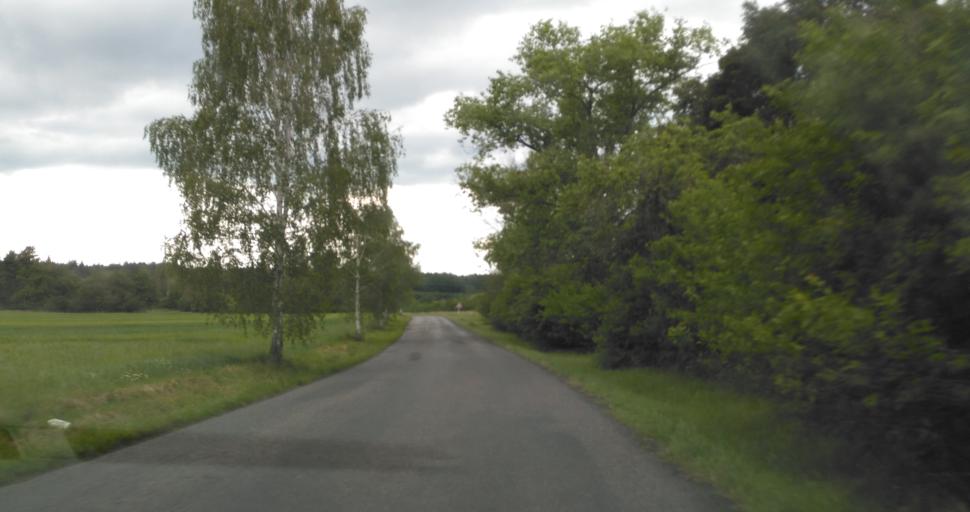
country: CZ
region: Central Bohemia
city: Zebrak
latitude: 49.9066
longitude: 13.8785
